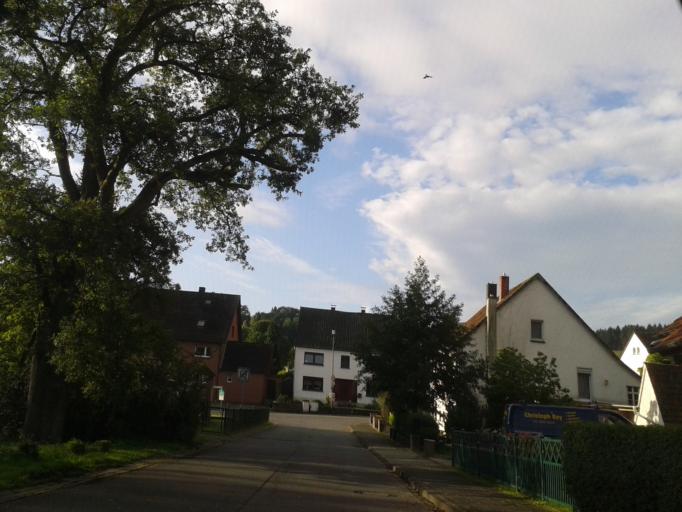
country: DE
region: North Rhine-Westphalia
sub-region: Regierungsbezirk Detmold
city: Dorentrup
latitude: 51.9968
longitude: 9.0490
